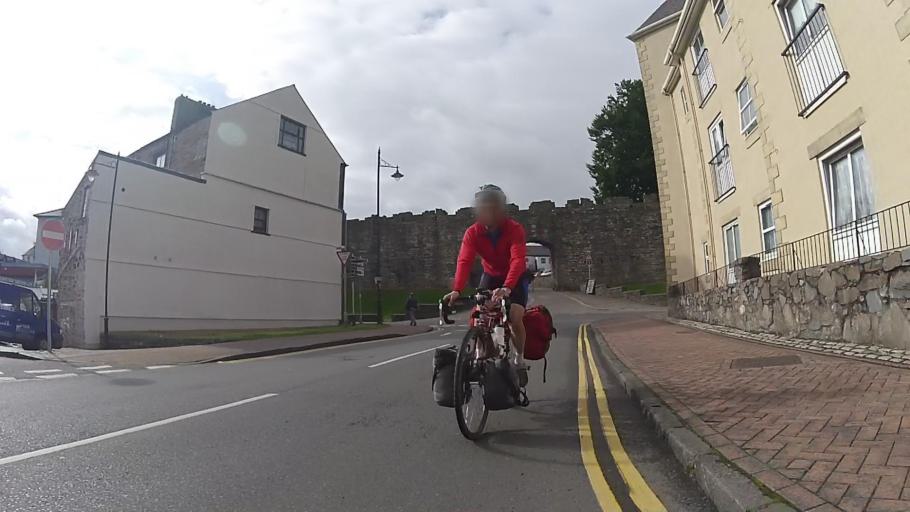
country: GB
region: Wales
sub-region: Gwynedd
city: Caernarfon
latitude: 53.1418
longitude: -4.2755
